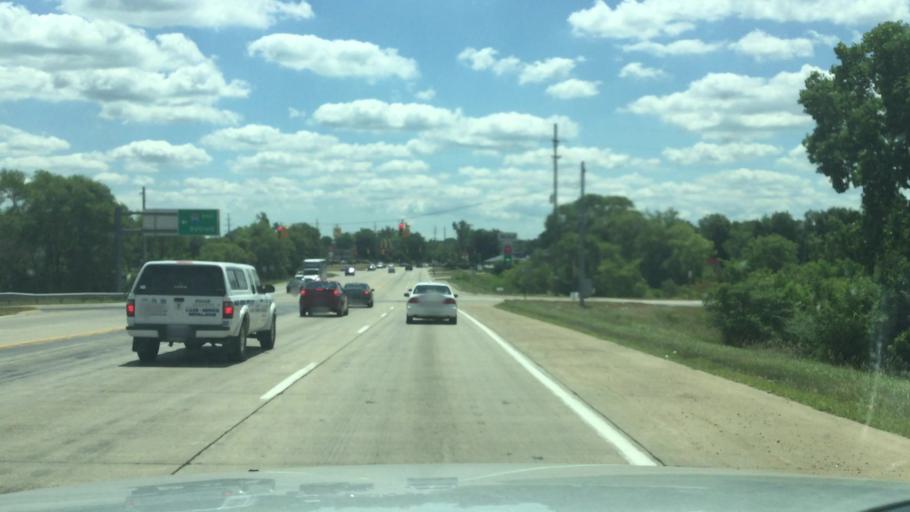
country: US
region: Michigan
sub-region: Wayne County
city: Belleville
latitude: 42.2175
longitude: -83.5454
